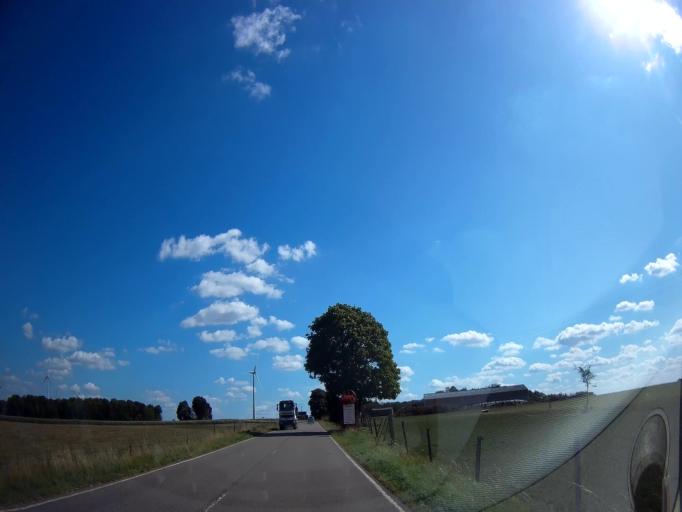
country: BE
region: Wallonia
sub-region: Province de Namur
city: Hastiere-Lavaux
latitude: 50.1832
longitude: 4.8538
